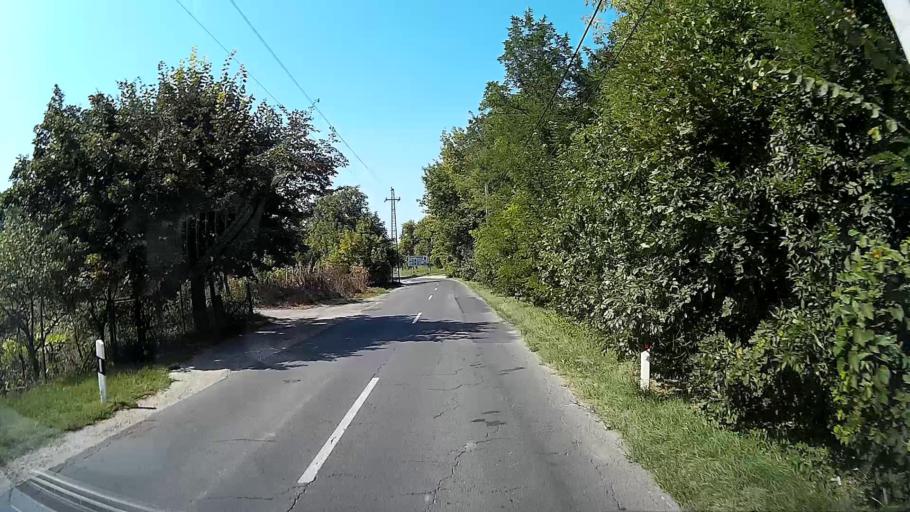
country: HU
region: Pest
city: Diosd
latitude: 47.4239
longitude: 18.9409
